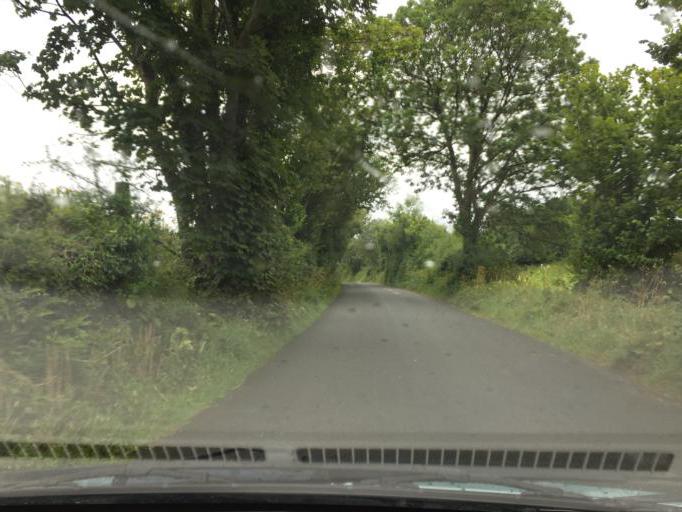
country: IE
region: Connaught
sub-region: Sligo
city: Sligo
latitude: 54.2319
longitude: -8.4598
